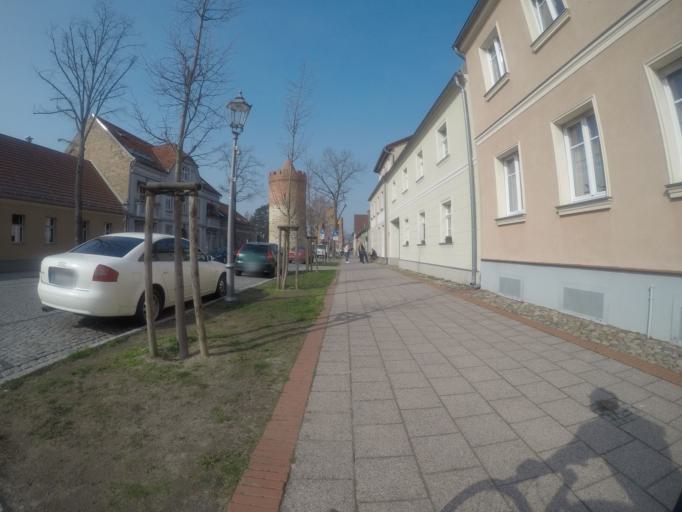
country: DE
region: Brandenburg
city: Mittenwalde
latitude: 52.2658
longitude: 13.5357
